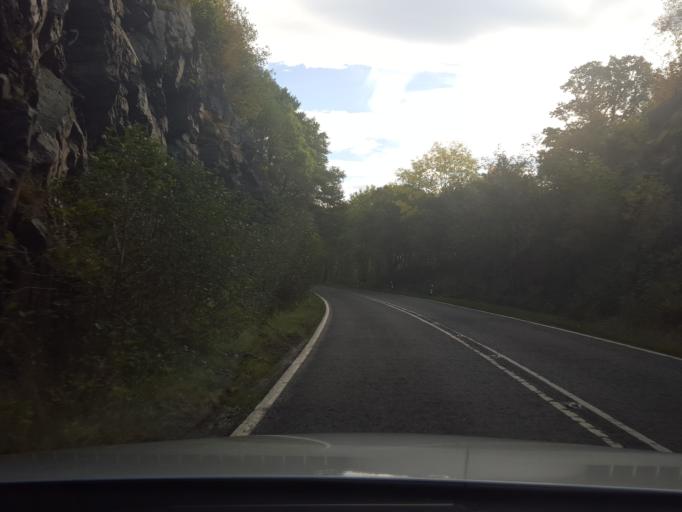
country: GB
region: Scotland
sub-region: Highland
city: Fort William
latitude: 57.2587
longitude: -5.4899
